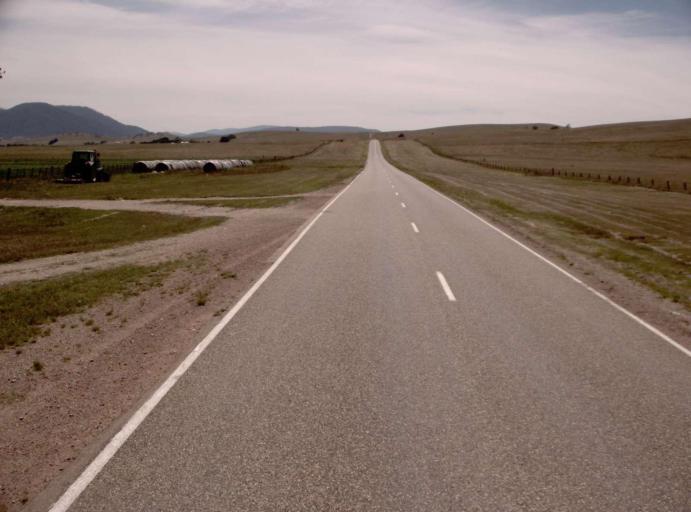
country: AU
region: Victoria
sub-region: Alpine
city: Mount Beauty
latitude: -36.9952
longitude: 147.6826
